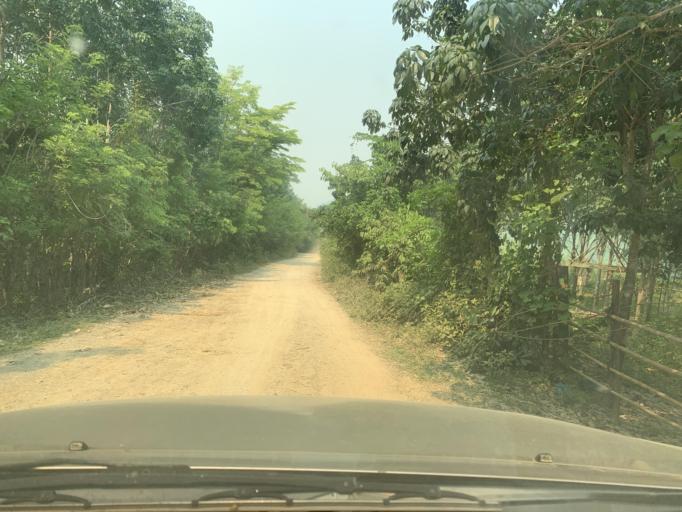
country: LA
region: Louangphabang
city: Louangphabang
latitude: 19.8955
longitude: 102.2531
